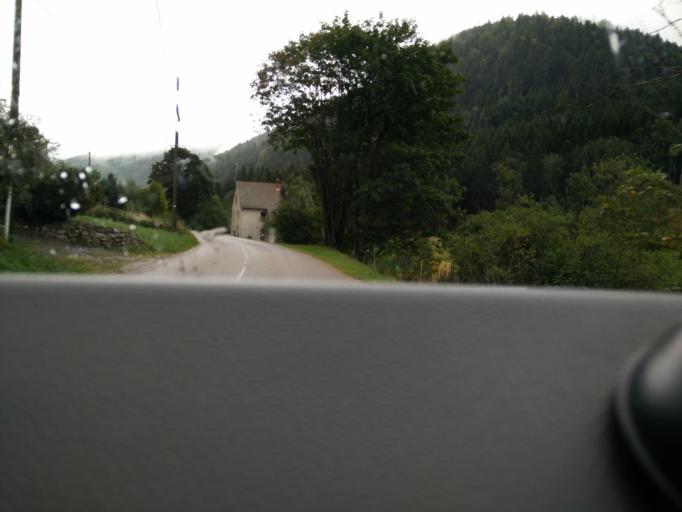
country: FR
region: Lorraine
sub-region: Departement des Vosges
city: Plainfaing
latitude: 48.1031
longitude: 7.0266
